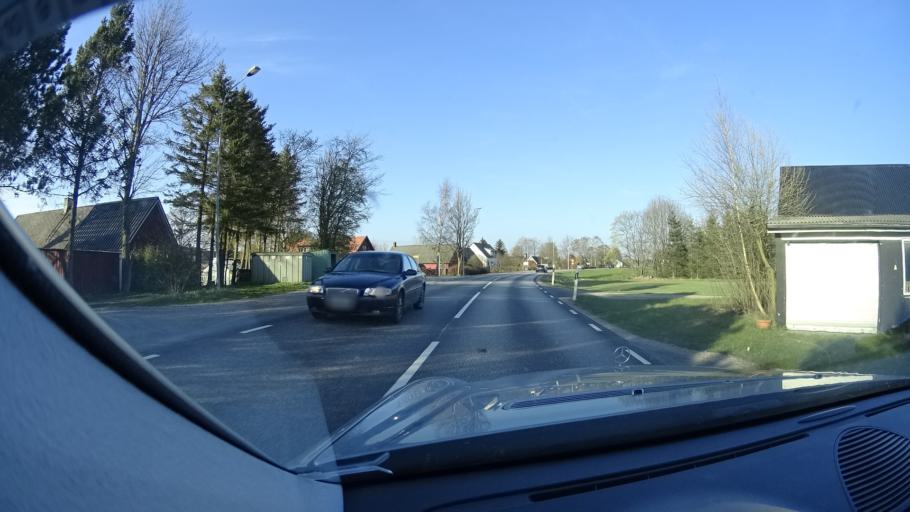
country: SE
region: Skane
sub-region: Eslovs Kommun
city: Eslov
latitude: 55.8505
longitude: 13.3464
